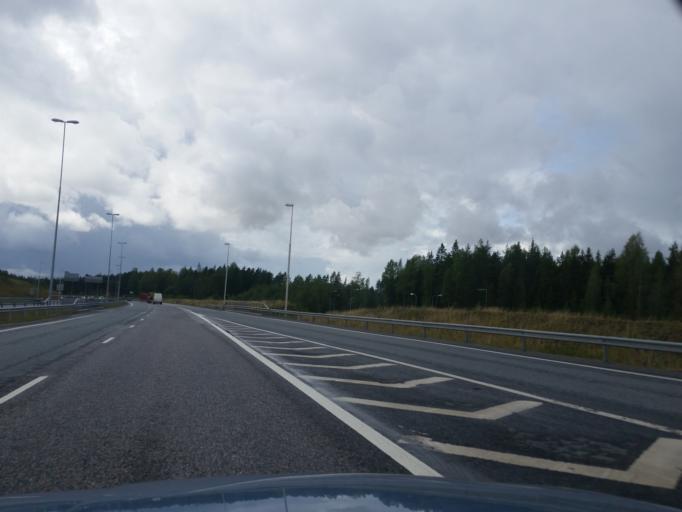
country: FI
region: Uusimaa
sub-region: Helsinki
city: Lohja
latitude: 60.3021
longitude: 24.2108
